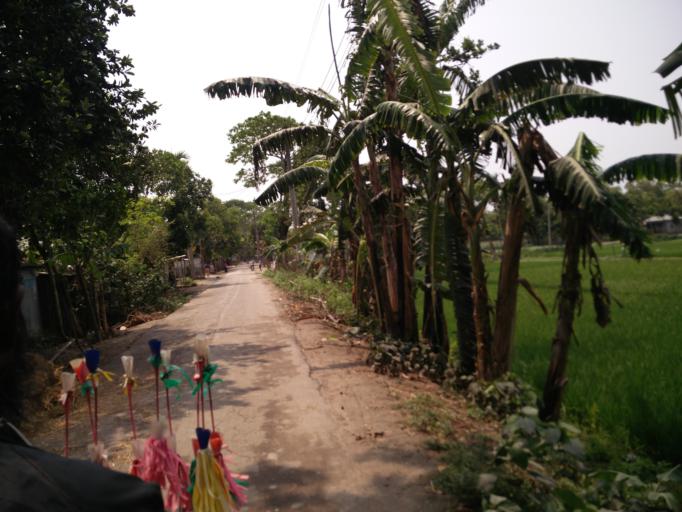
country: BD
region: Dhaka
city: Sherpur
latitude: 24.9517
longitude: 90.1643
